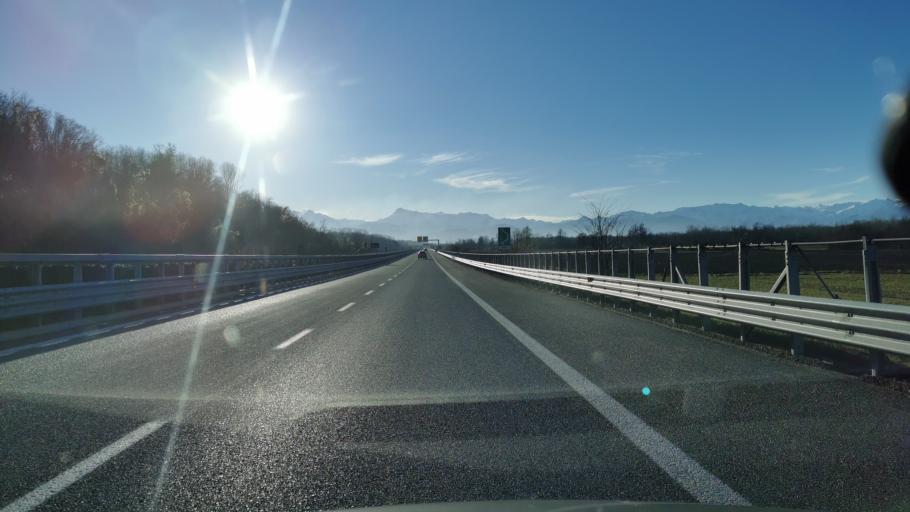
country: IT
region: Piedmont
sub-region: Provincia di Cuneo
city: Castelletto Stura
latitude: 44.4412
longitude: 7.6285
